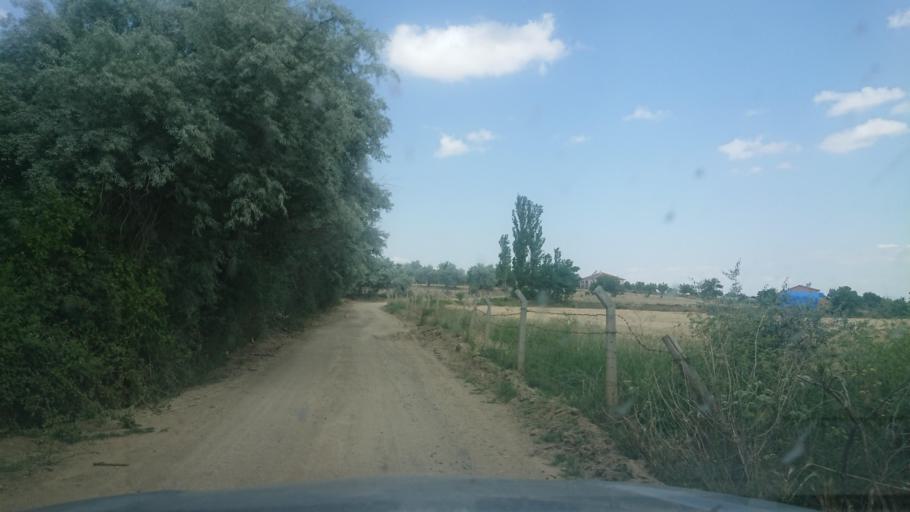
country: TR
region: Aksaray
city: Agacoren
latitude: 38.9331
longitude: 33.9538
